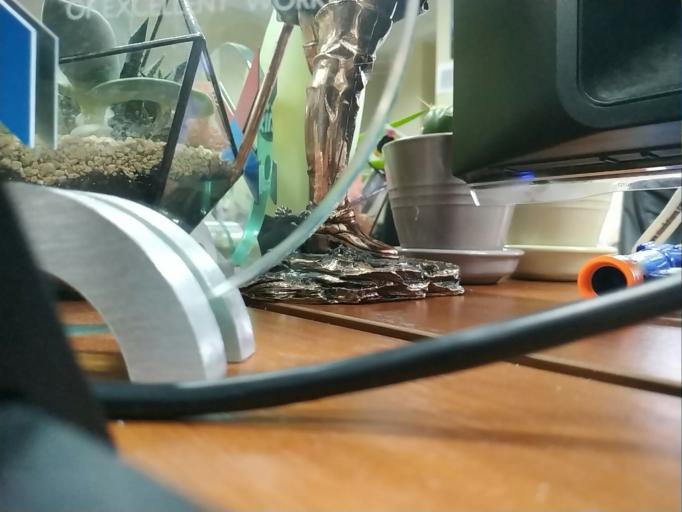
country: RU
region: Moskovskaya
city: Yermolino
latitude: 56.1389
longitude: 37.4414
